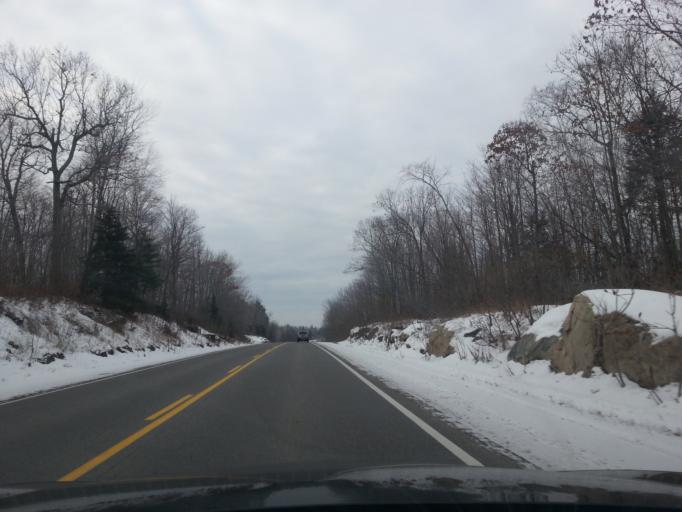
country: CA
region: Ontario
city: Perth
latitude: 44.8086
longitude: -76.6421
